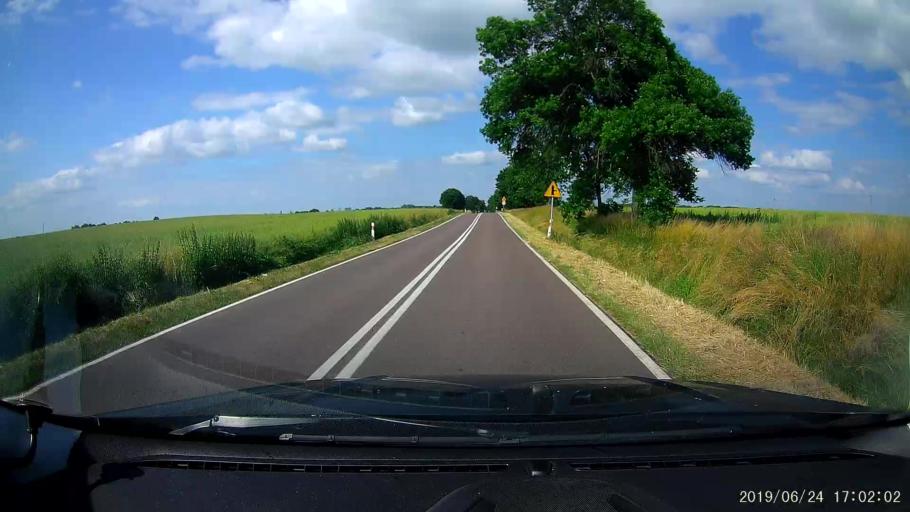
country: PL
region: Lublin Voivodeship
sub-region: Powiat tomaszowski
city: Telatyn
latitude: 50.5466
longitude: 23.9280
